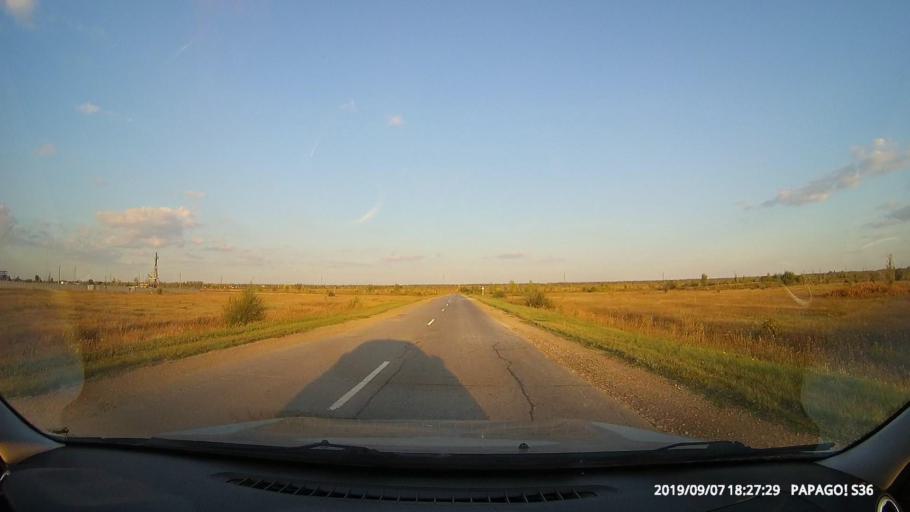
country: RU
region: Samara
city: Chapayevsk
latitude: 52.9936
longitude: 49.7767
